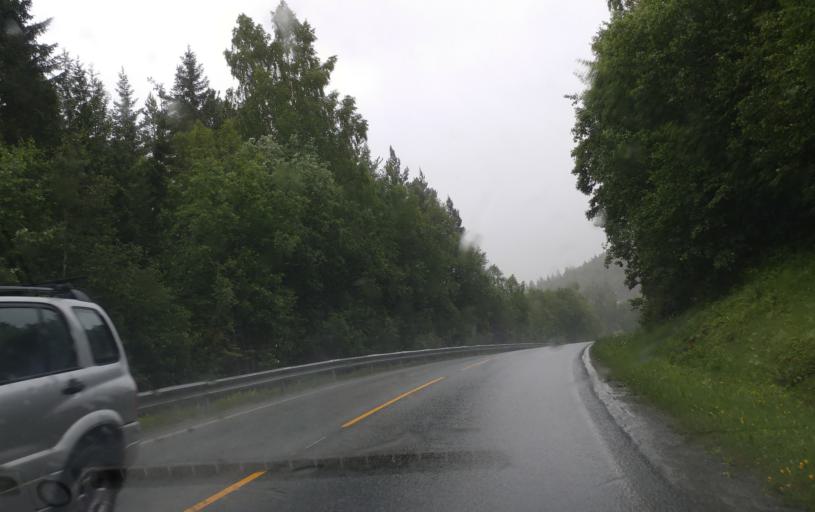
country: NO
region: Nord-Trondelag
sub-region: Stjordal
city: Stjordalshalsen
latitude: 63.3999
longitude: 10.9488
